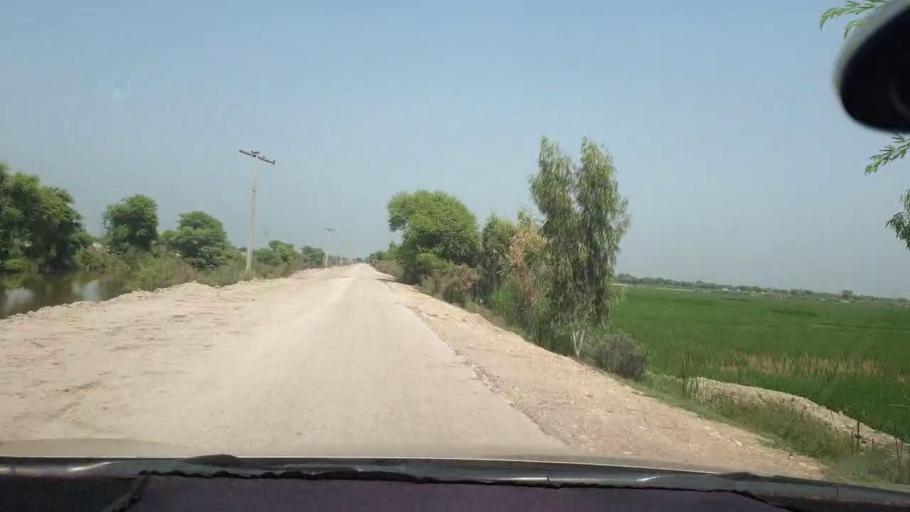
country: PK
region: Sindh
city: Kambar
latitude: 27.6621
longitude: 67.8873
